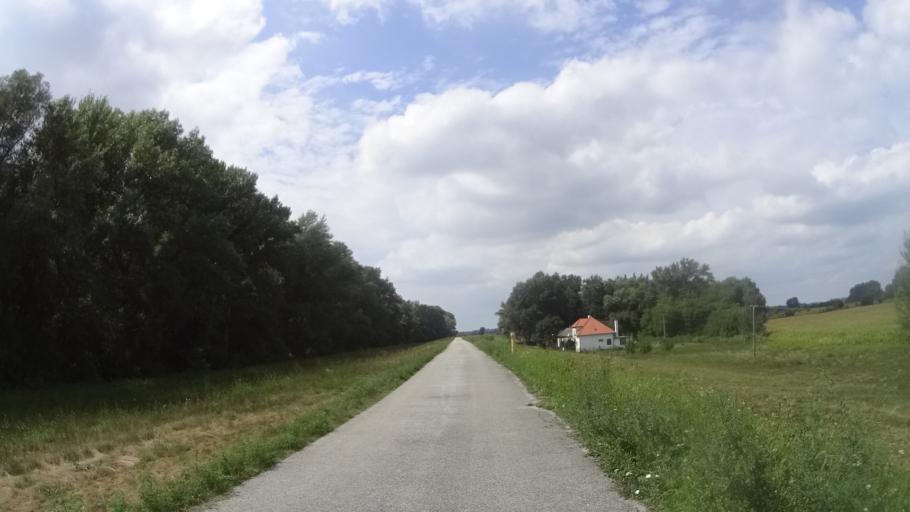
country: SK
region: Trnavsky
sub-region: Okres Dunajska Streda
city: Velky Meder
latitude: 47.7911
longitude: 17.6898
